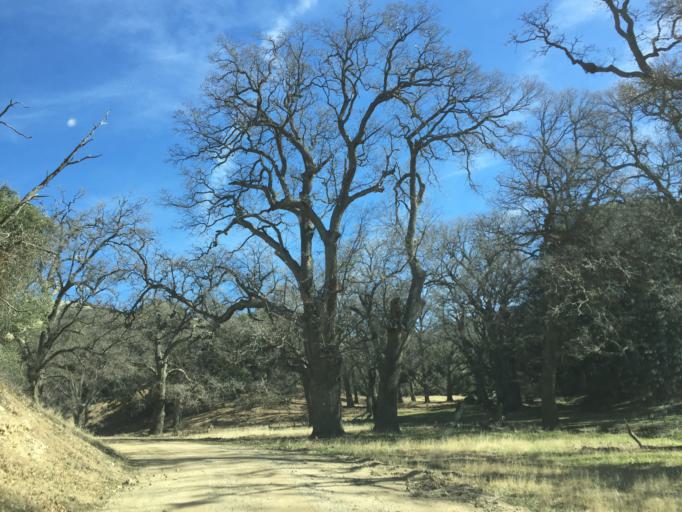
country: US
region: California
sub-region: Kern County
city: Stallion Springs
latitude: 34.9155
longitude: -118.6842
